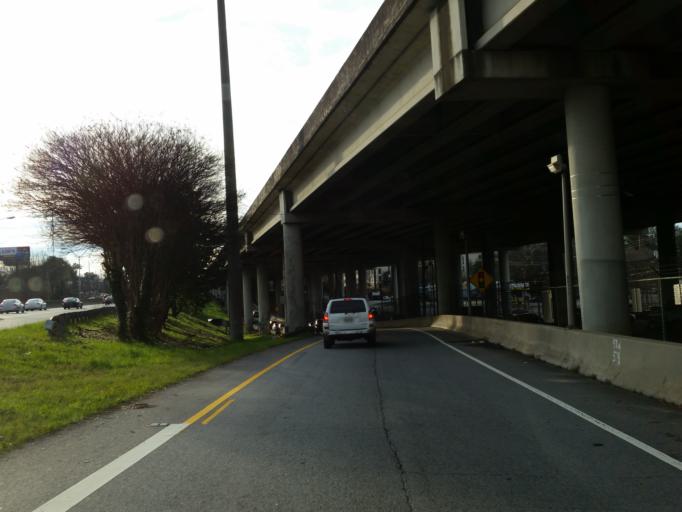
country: US
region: Georgia
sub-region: DeKalb County
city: Druid Hills
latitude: 33.8118
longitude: -84.3697
